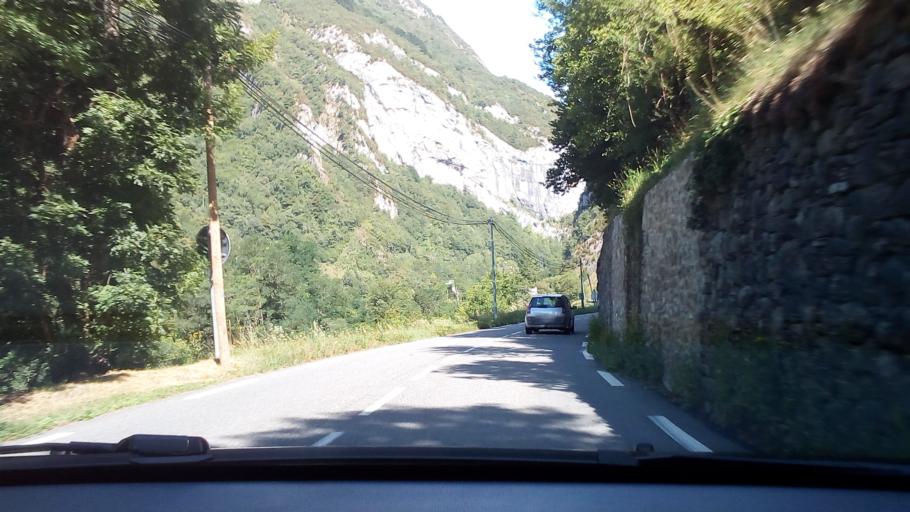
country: ES
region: Aragon
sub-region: Provincia de Huesca
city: Canfranc
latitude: 42.8784
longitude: -0.5573
